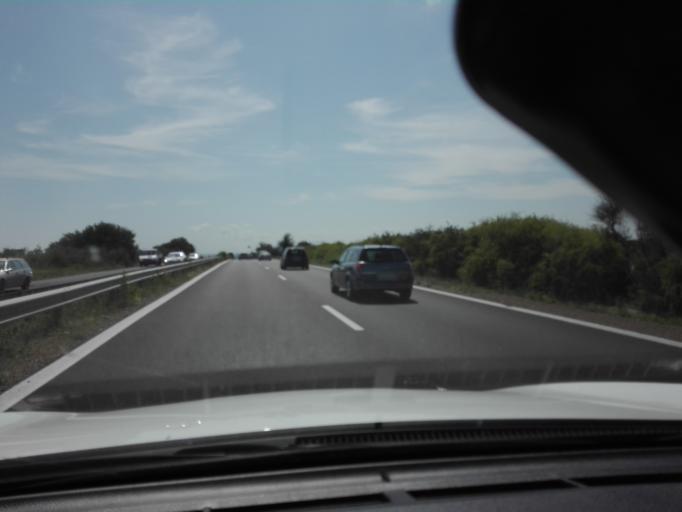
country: BG
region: Burgas
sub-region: Obshtina Burgas
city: Burgas
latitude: 42.5609
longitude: 27.4228
